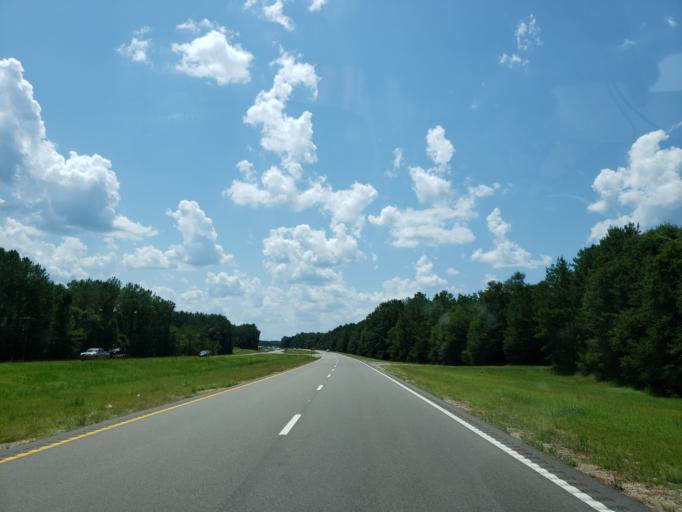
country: US
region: Mississippi
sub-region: Greene County
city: Leakesville
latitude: 31.1078
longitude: -88.7916
